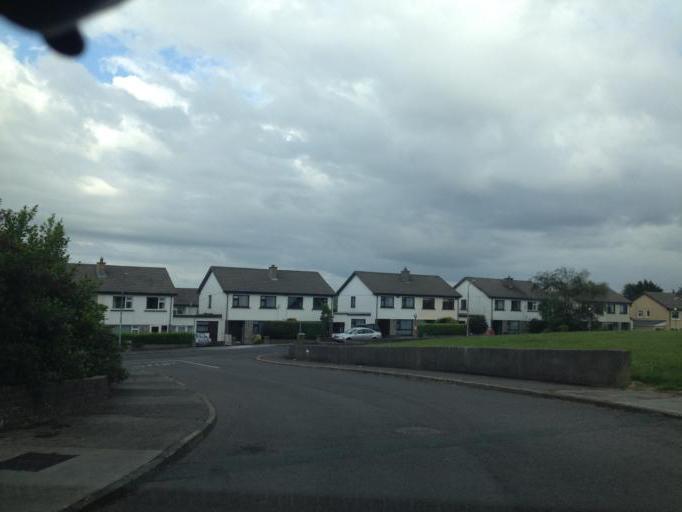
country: IE
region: Connaught
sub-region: Sligo
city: Sligo
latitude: 54.2809
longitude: -8.4825
